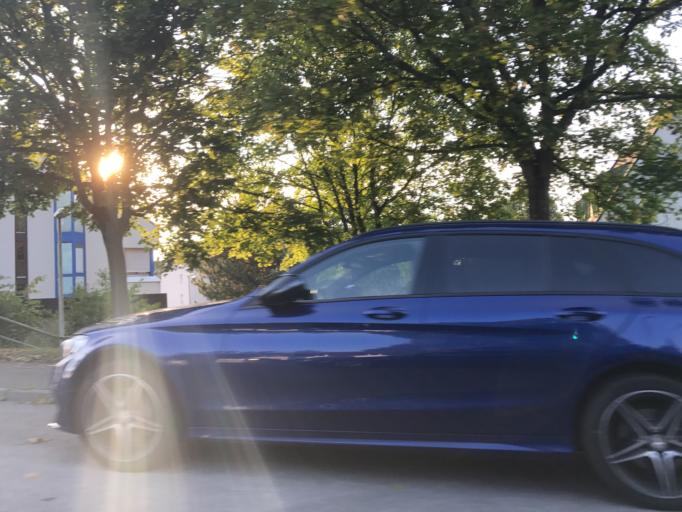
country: DE
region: Baden-Wuerttemberg
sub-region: Regierungsbezirk Stuttgart
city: Korntal
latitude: 48.8248
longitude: 9.1229
